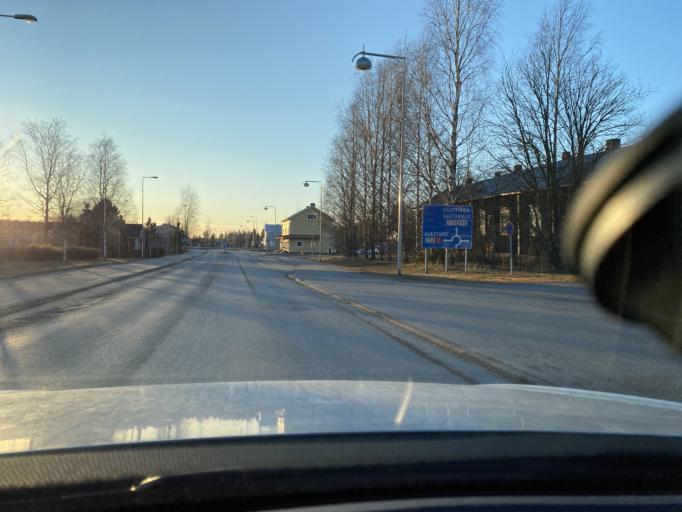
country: FI
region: Pirkanmaa
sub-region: Lounais-Pirkanmaa
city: Punkalaidun
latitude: 61.1111
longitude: 23.1102
